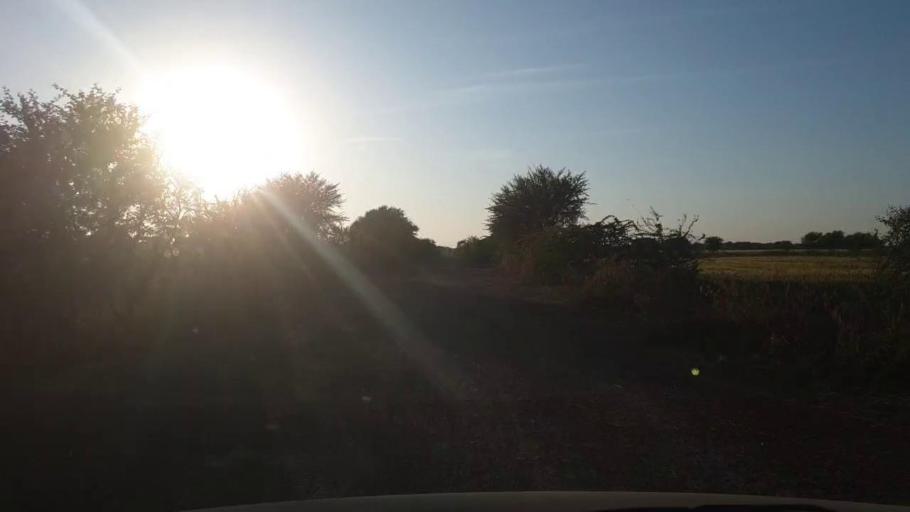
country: PK
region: Sindh
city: Dhoro Naro
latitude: 25.3634
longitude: 69.5682
